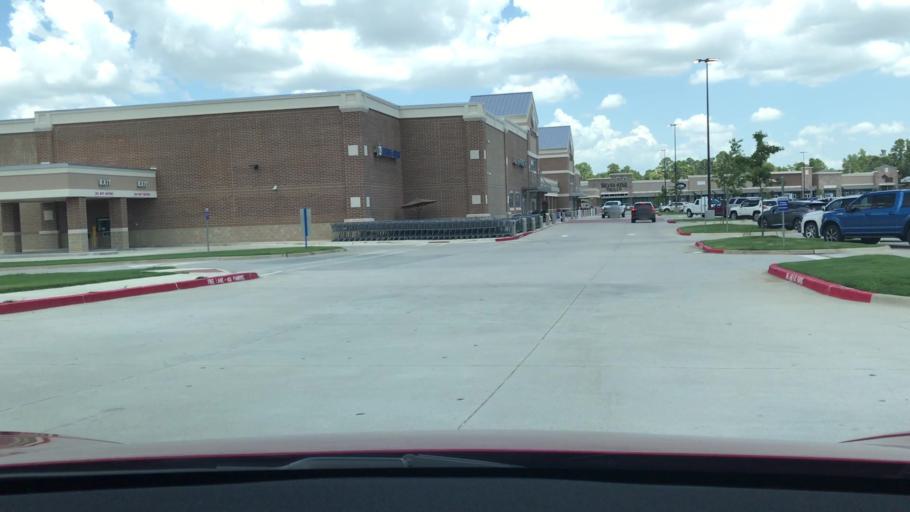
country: US
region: Louisiana
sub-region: Bossier Parish
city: Bossier City
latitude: 32.3930
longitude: -93.7281
